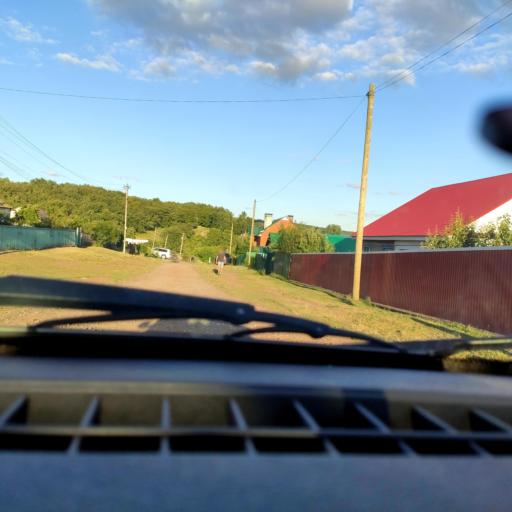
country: RU
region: Bashkortostan
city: Avdon
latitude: 54.6368
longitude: 55.5916
